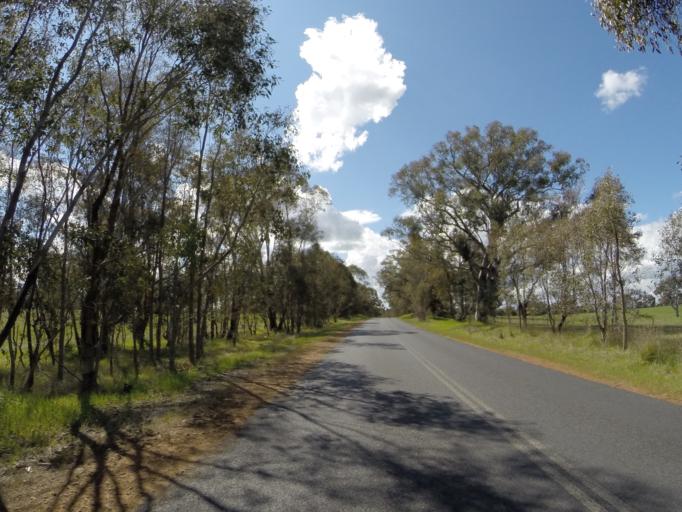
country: AU
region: New South Wales
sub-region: Yass Valley
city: Yass
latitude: -34.9793
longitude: 148.8556
